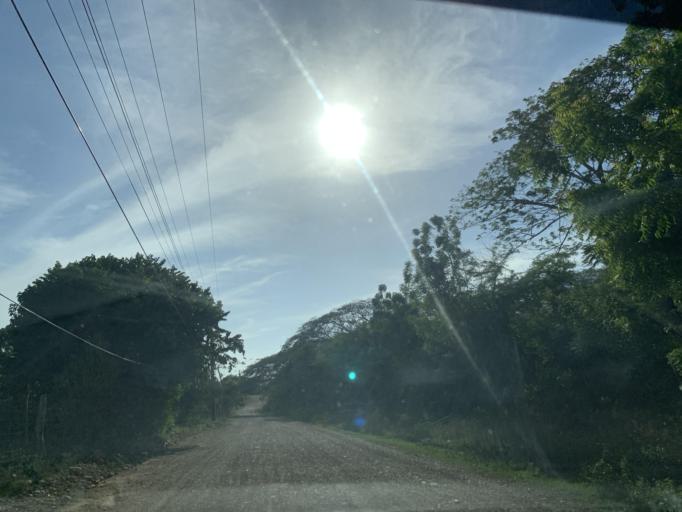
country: DO
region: Puerto Plata
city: Luperon
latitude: 19.8787
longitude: -70.9282
